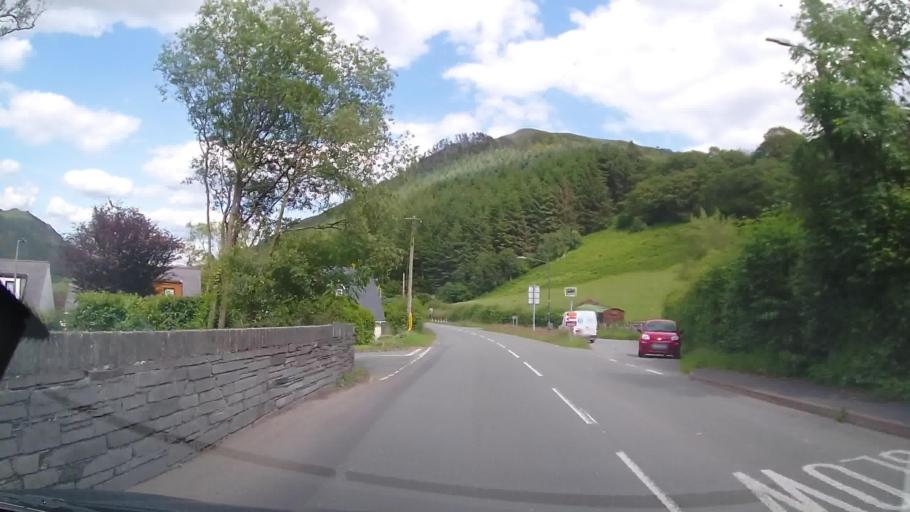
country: GB
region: Wales
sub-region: Gwynedd
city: Corris
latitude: 52.6446
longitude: -3.9548
